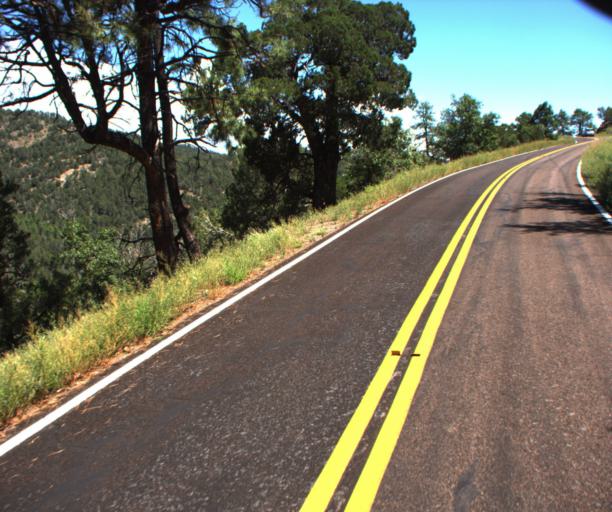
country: US
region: Arizona
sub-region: Greenlee County
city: Morenci
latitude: 33.4094
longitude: -109.3553
